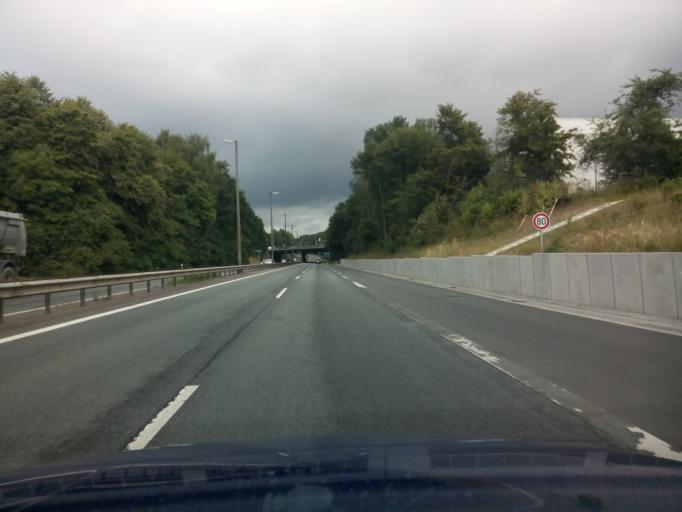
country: DE
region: Lower Saxony
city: Lemwerder
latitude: 53.1732
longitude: 8.6537
